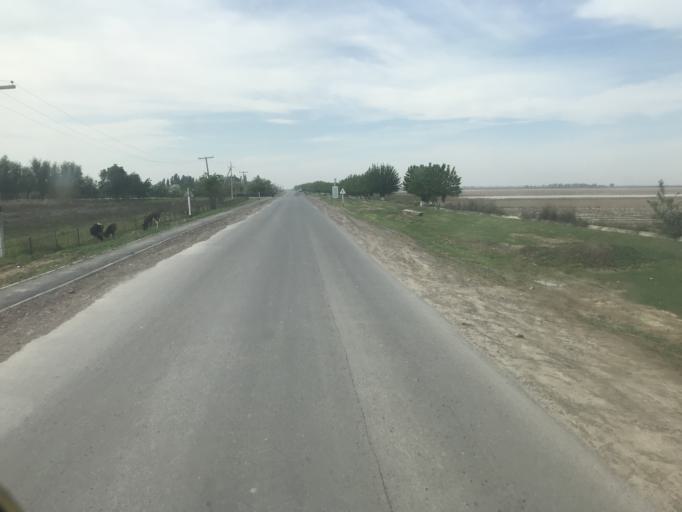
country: KZ
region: Ongtustik Qazaqstan
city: Asykata
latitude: 40.9944
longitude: 68.2111
